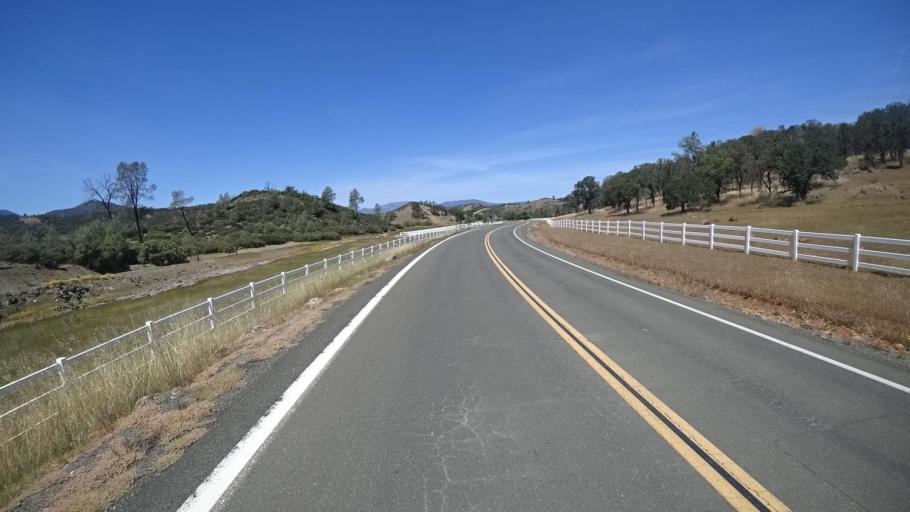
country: US
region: California
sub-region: Lake County
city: Hidden Valley Lake
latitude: 38.7239
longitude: -122.5112
